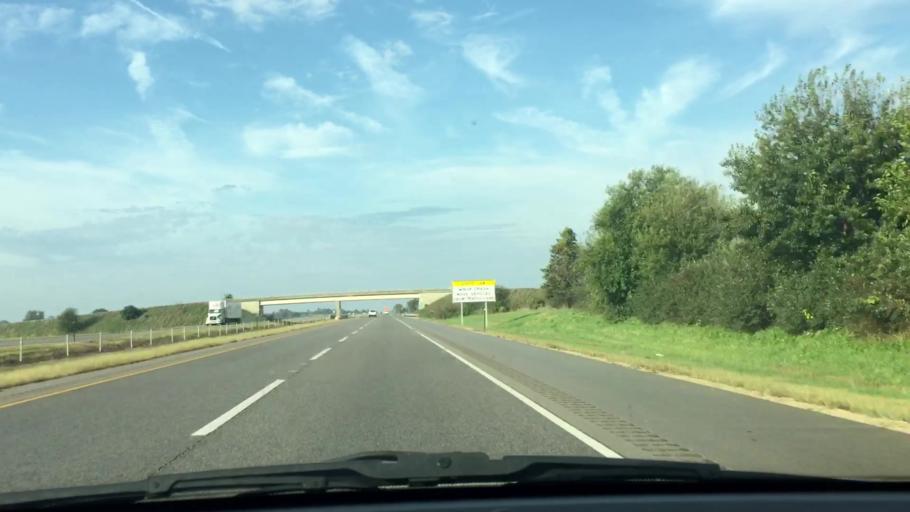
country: US
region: Illinois
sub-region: Ogle County
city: Rochelle
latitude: 41.8703
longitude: -89.1656
